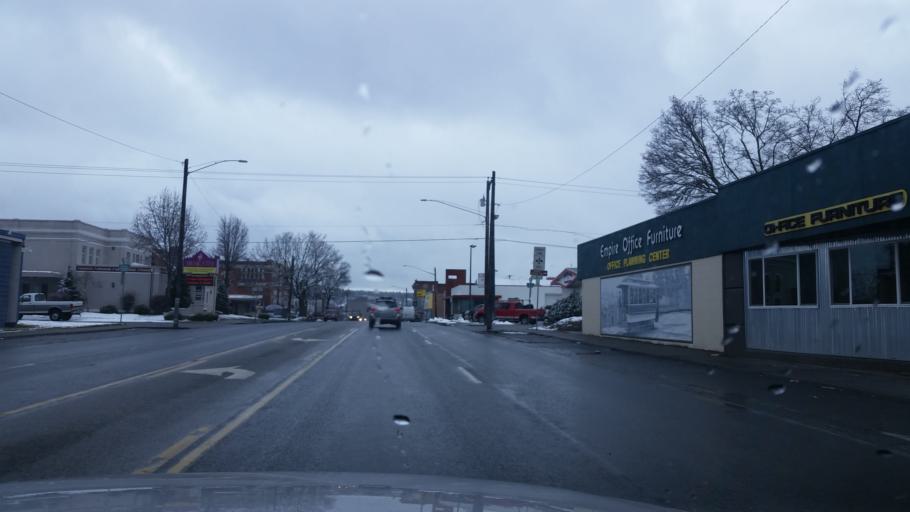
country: US
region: Washington
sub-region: Spokane County
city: Spokane
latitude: 47.6707
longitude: -117.4267
